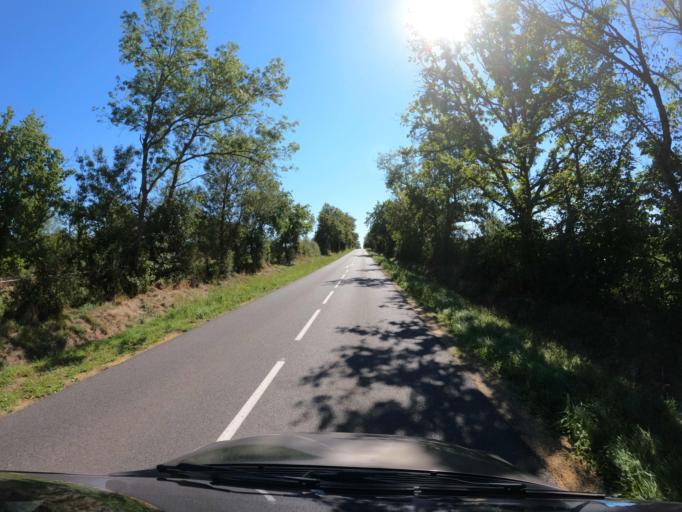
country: FR
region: Poitou-Charentes
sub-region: Departement de la Vienne
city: Saulge
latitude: 46.3944
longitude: 0.9032
